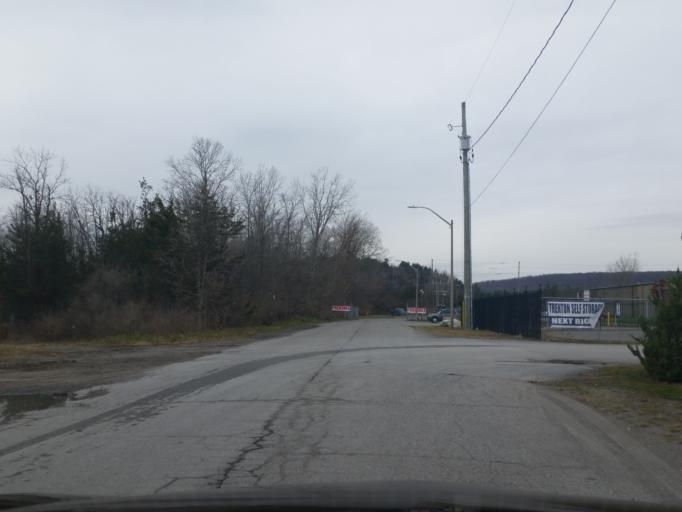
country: CA
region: Ontario
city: Quinte West
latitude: 44.1272
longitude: -77.5882
